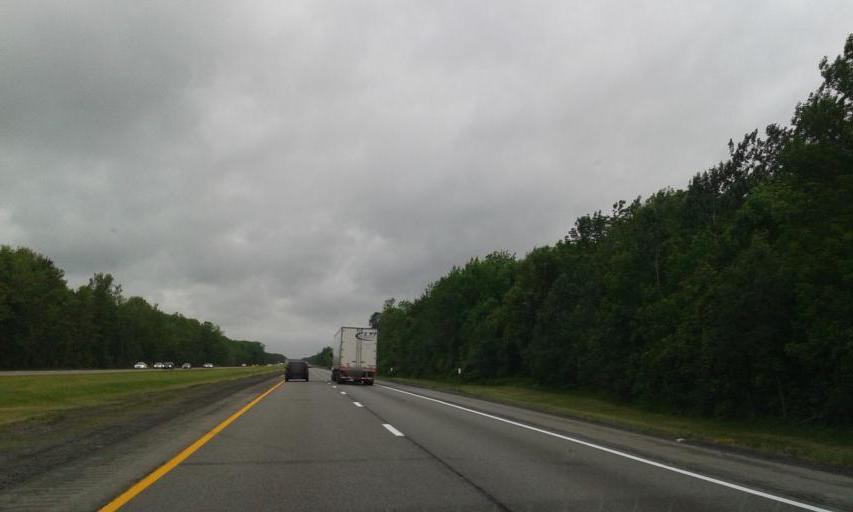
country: US
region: New York
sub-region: Erie County
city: Akron
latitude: 42.9912
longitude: -78.4399
